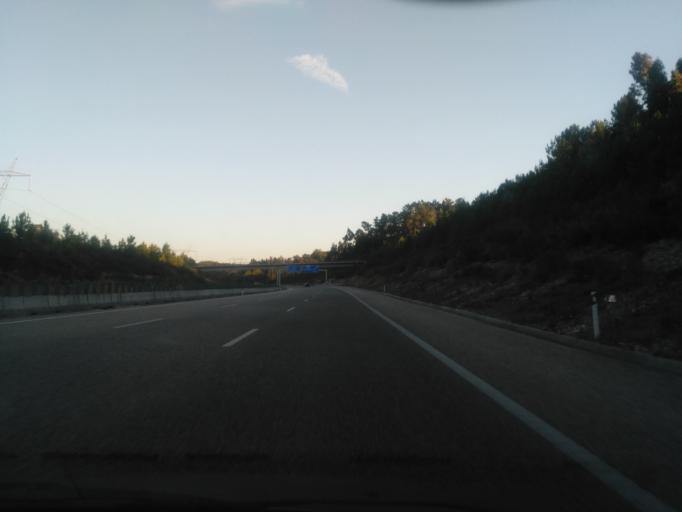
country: PT
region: Leiria
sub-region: Pombal
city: Lourical
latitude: 39.9586
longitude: -8.7750
